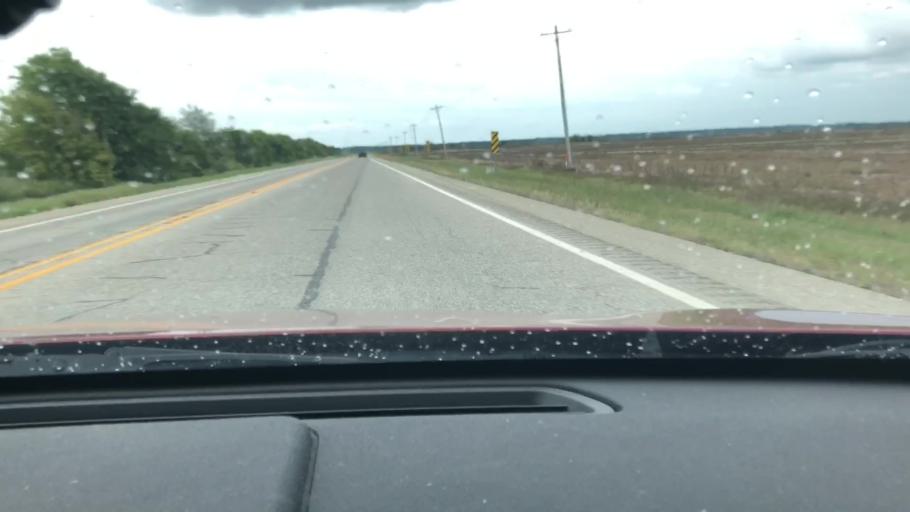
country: US
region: Arkansas
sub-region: Lafayette County
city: Lewisville
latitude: 33.4120
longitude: -93.7762
